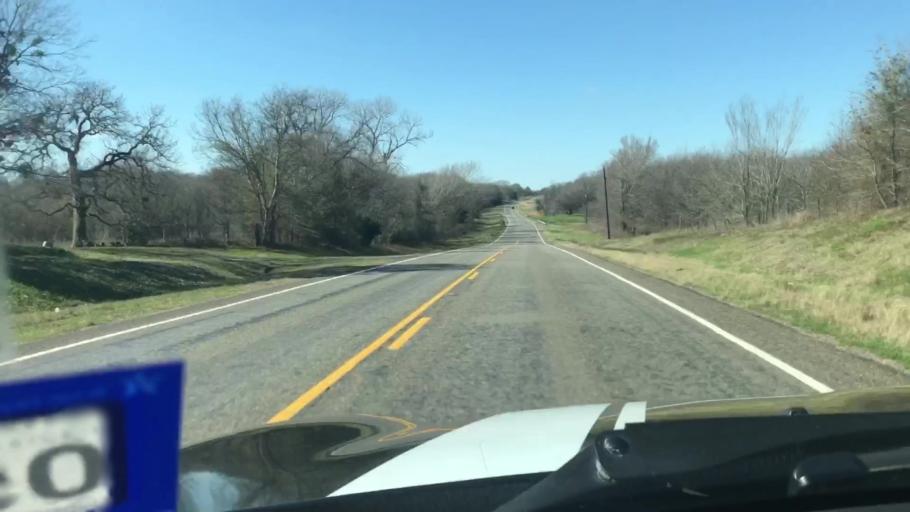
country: US
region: Texas
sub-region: Robertson County
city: Calvert
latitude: 30.8848
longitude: -96.7591
